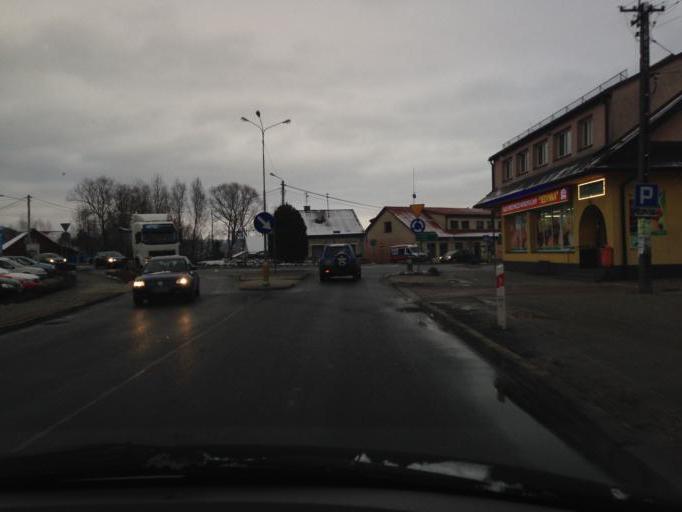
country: PL
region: Lesser Poland Voivodeship
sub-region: Powiat tarnowski
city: Gromnik
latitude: 49.8383
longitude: 20.9605
